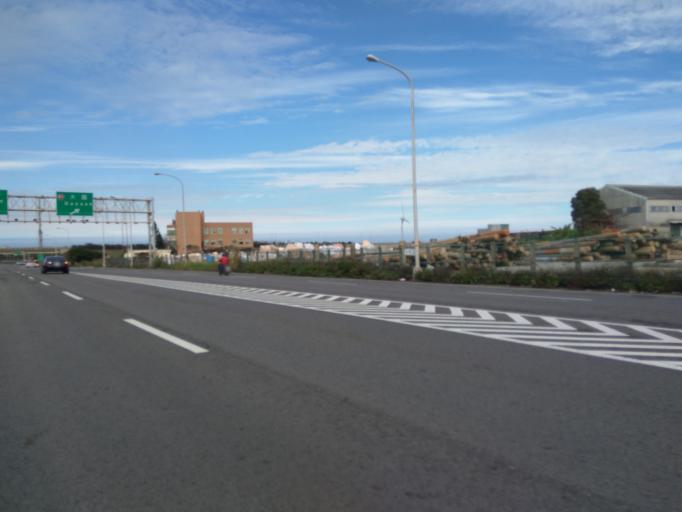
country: TW
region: Taiwan
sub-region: Hsinchu
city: Zhubei
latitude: 25.0278
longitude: 121.0568
